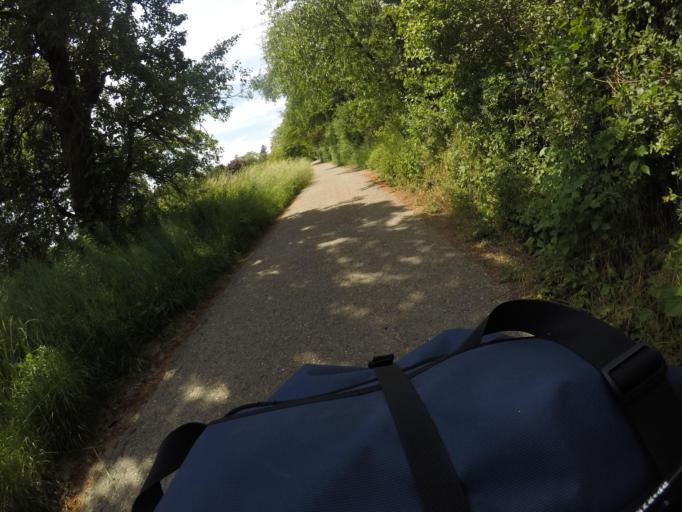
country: DE
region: Baden-Wuerttemberg
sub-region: Karlsruhe Region
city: Konigsbach-Stein
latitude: 48.9661
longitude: 8.5354
